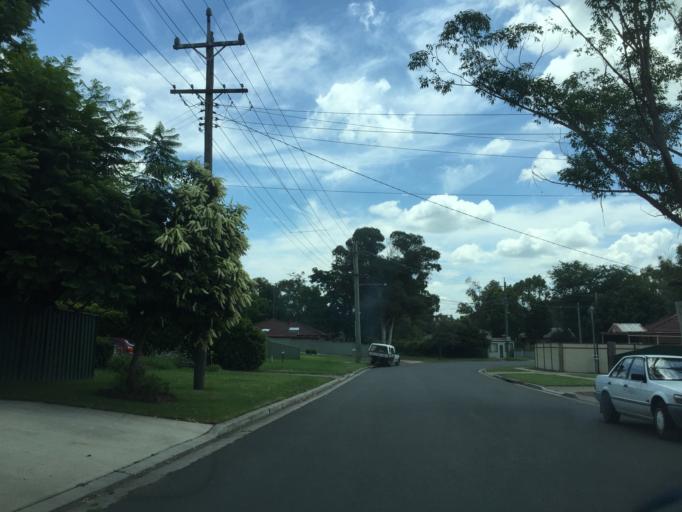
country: AU
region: New South Wales
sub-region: Blacktown
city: Riverstone
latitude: -33.6988
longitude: 150.8694
